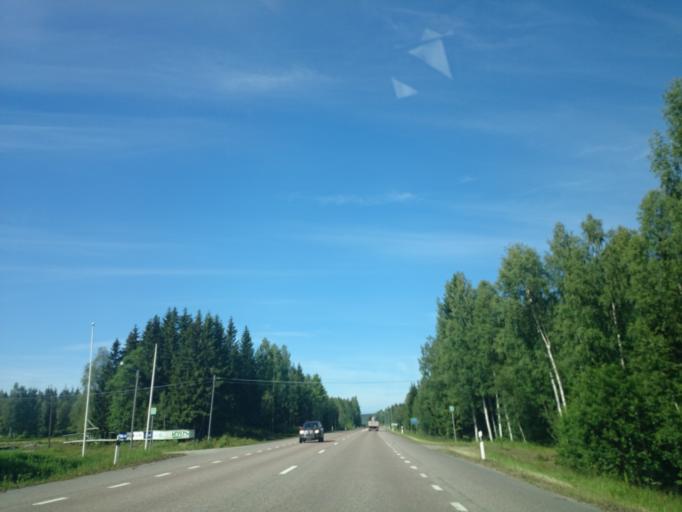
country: SE
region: Vaesternorrland
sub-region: Sundsvalls Kommun
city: Vi
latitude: 62.3777
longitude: 17.1413
